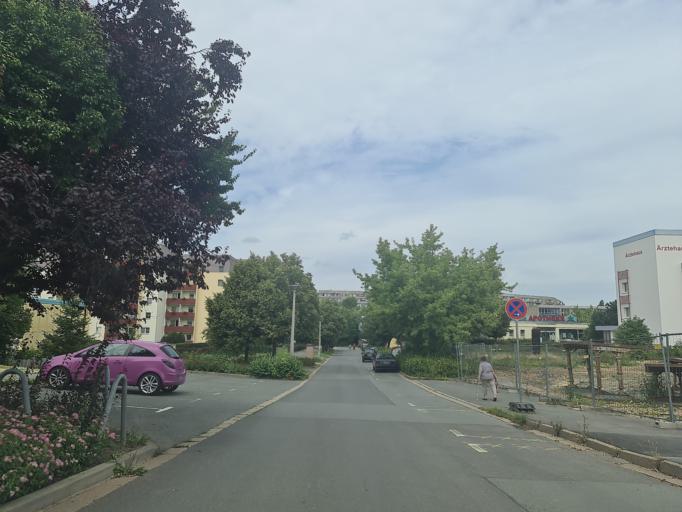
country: DE
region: Saxony
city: Plauen
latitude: 50.4986
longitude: 12.1630
